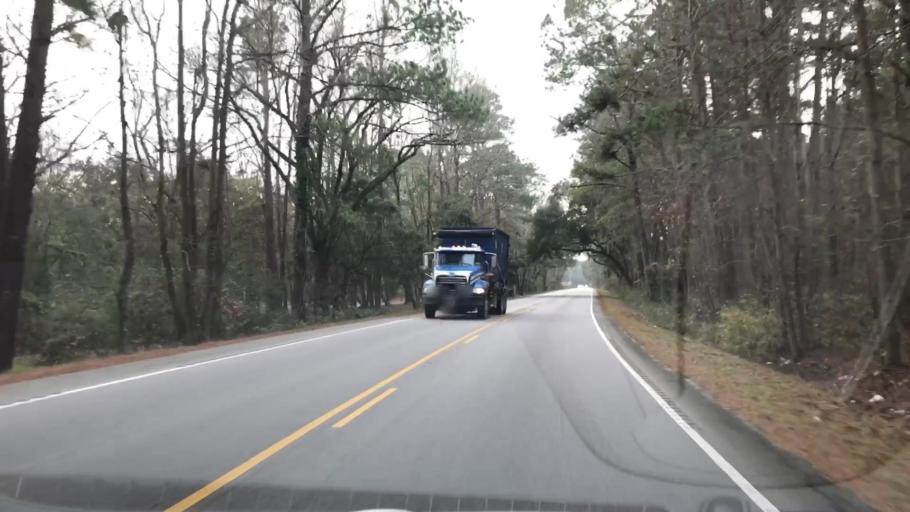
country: US
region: South Carolina
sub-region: Jasper County
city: Ridgeland
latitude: 32.5683
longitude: -80.9181
